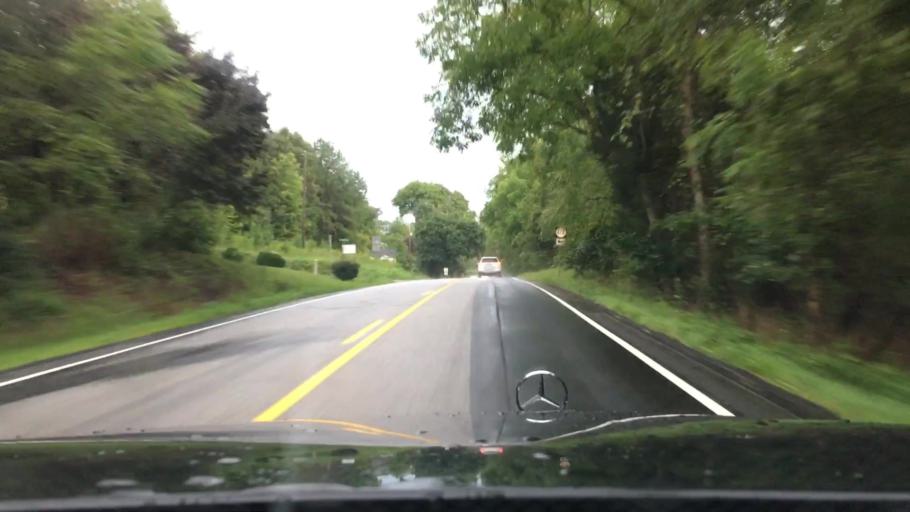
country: US
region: Virginia
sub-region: Amherst County
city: Amherst
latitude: 37.6678
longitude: -79.0122
